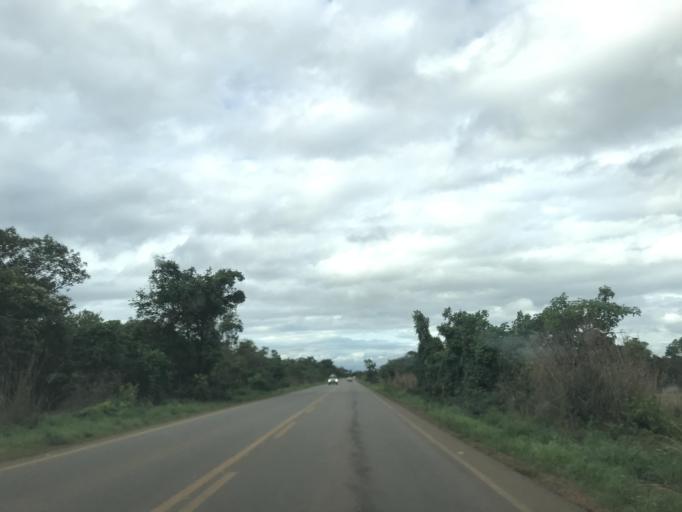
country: BR
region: Goias
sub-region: Vianopolis
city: Vianopolis
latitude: -16.7387
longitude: -48.4474
